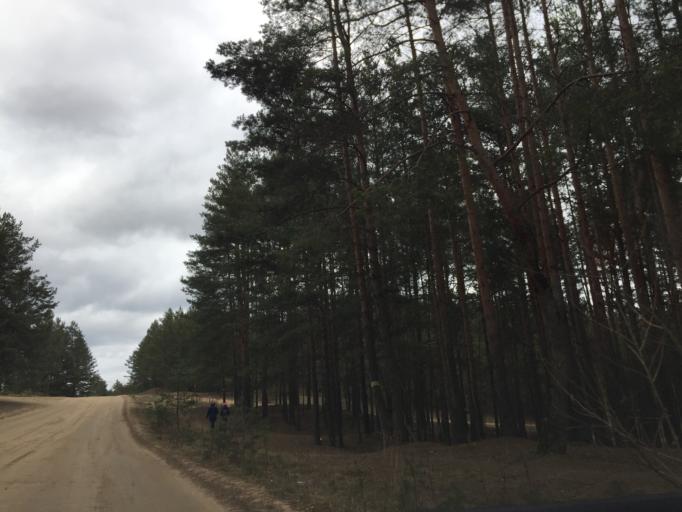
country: LV
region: Daugavpils
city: Daugavpils
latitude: 55.9080
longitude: 26.5384
